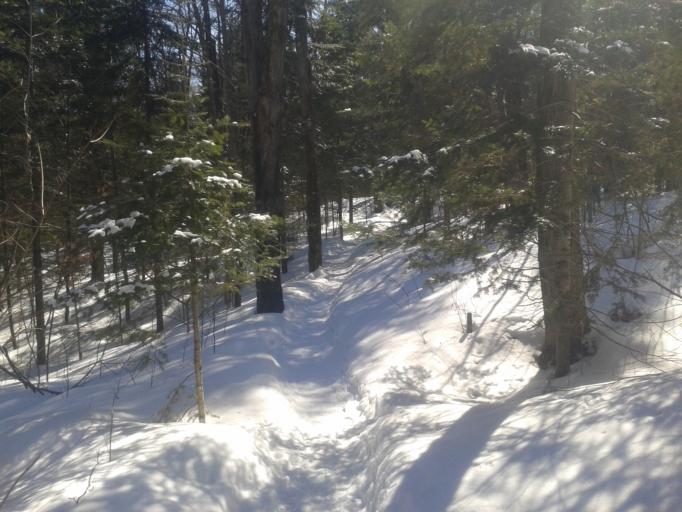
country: CA
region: Ontario
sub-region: Nipissing District
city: North Bay
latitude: 46.3419
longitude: -79.4970
